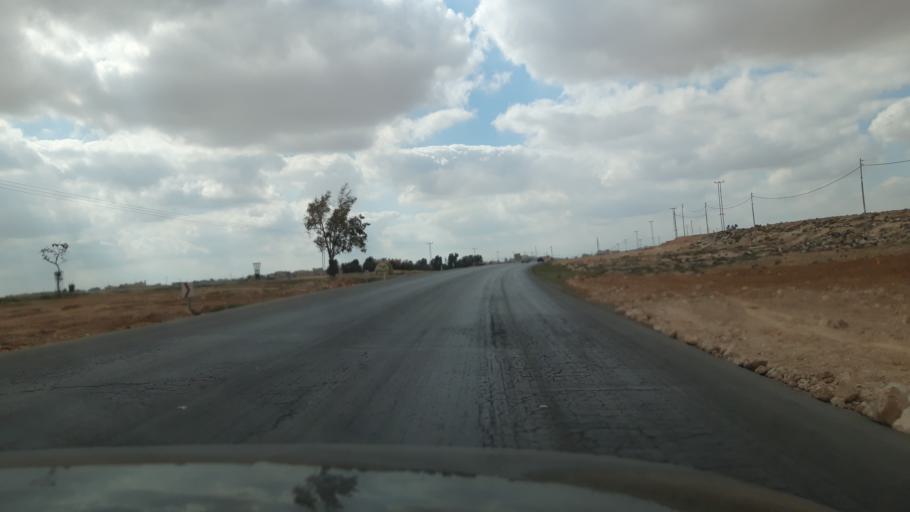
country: JO
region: Amman
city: Sahab
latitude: 31.8023
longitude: 36.1333
